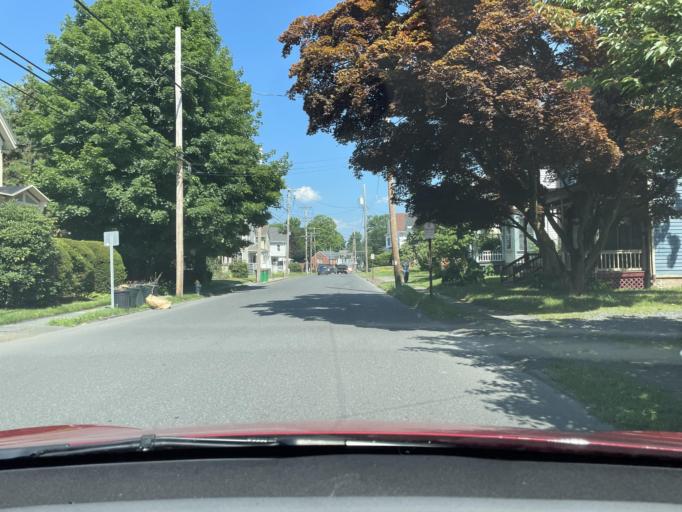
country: US
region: New York
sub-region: Ulster County
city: Kingston
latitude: 41.9320
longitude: -74.0231
